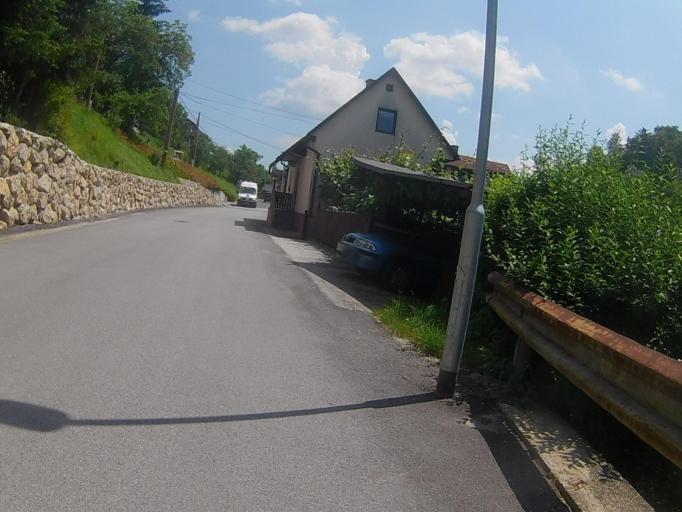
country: SI
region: Maribor
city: Kamnica
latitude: 46.5744
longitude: 15.6084
